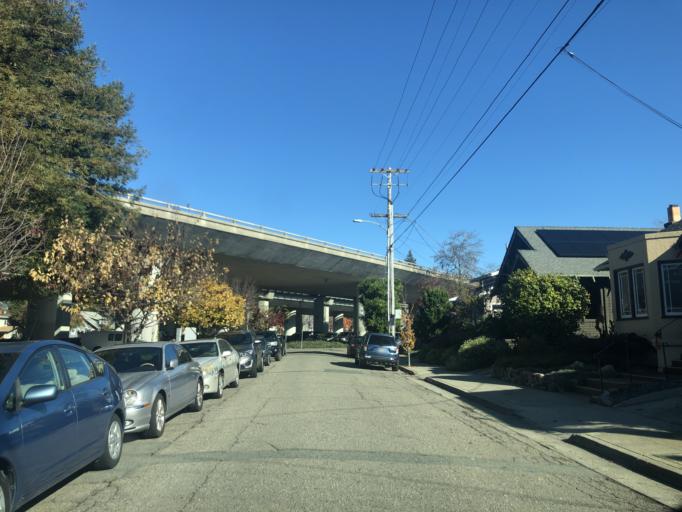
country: US
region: California
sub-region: Alameda County
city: Piedmont
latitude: 37.8430
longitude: -122.2542
